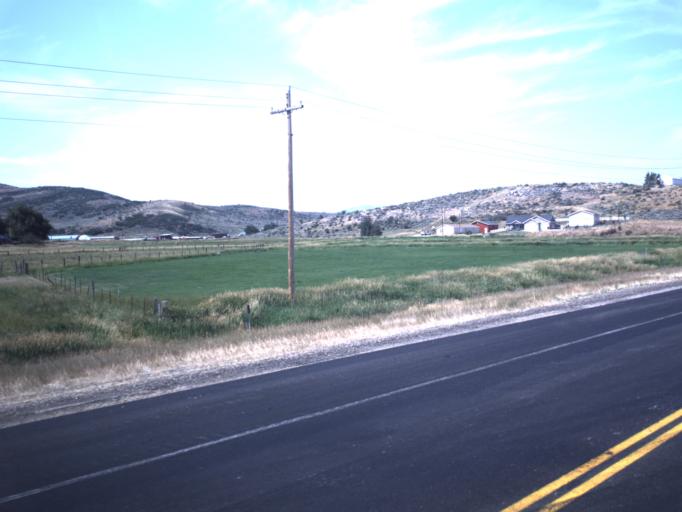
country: US
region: Utah
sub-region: Summit County
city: Kamas
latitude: 40.6400
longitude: -111.3106
